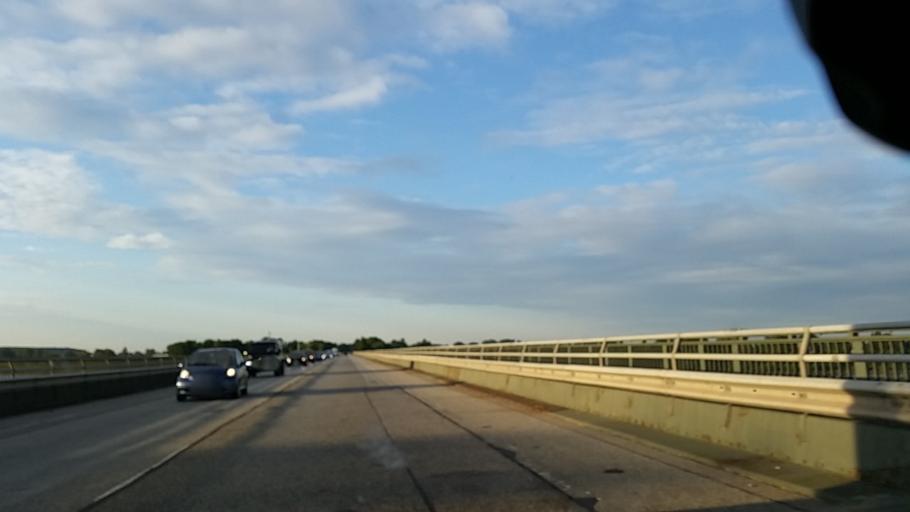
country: DE
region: Lower Saxony
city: Marschacht
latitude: 53.4267
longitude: 10.3355
